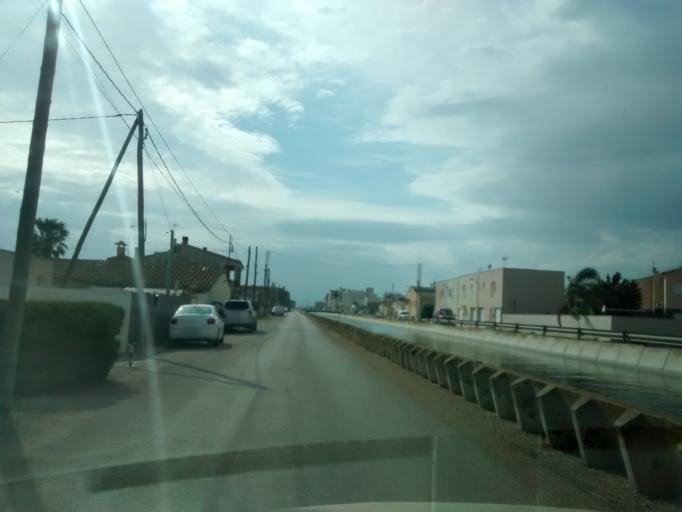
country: ES
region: Catalonia
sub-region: Provincia de Tarragona
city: Deltebre
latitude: 40.7029
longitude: 0.7226
